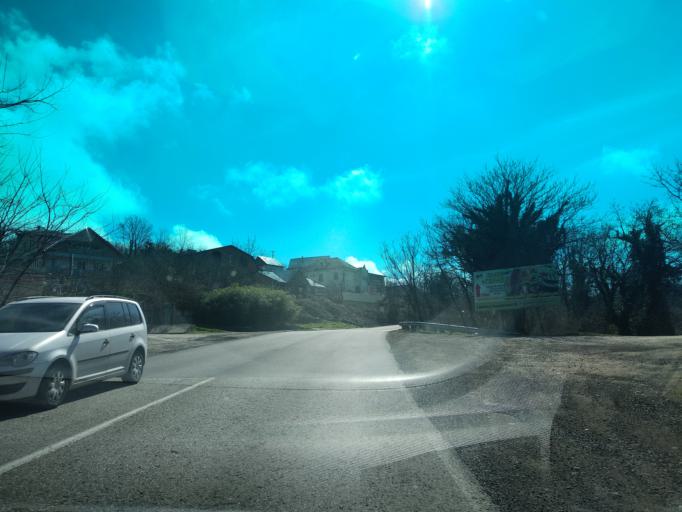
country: RU
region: Krasnodarskiy
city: Tuapse
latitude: 44.0901
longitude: 39.1225
